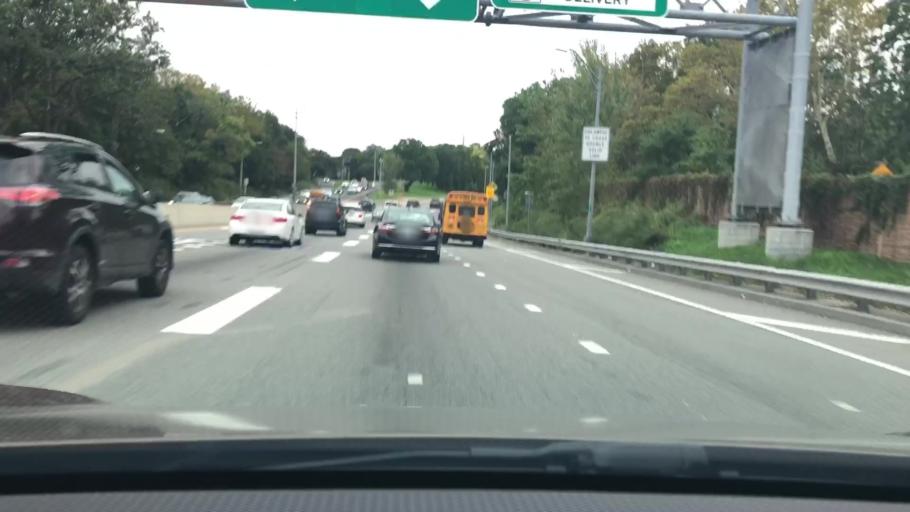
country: US
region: New York
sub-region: Bronx
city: The Bronx
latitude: 40.7934
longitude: -73.8243
